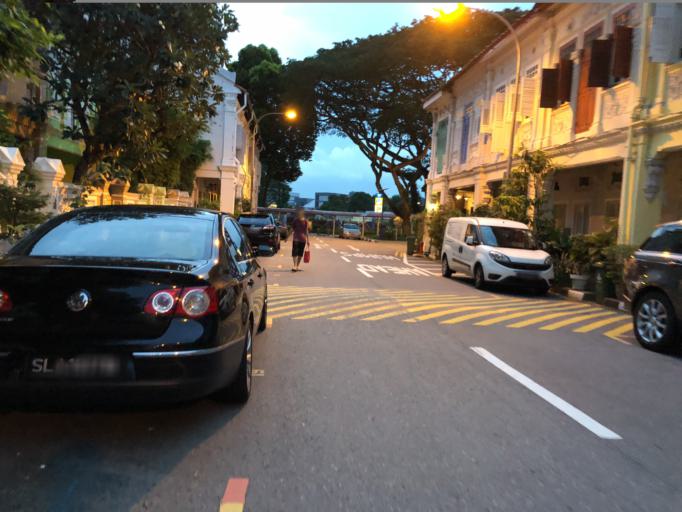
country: SG
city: Singapore
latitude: 1.2760
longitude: 103.8360
